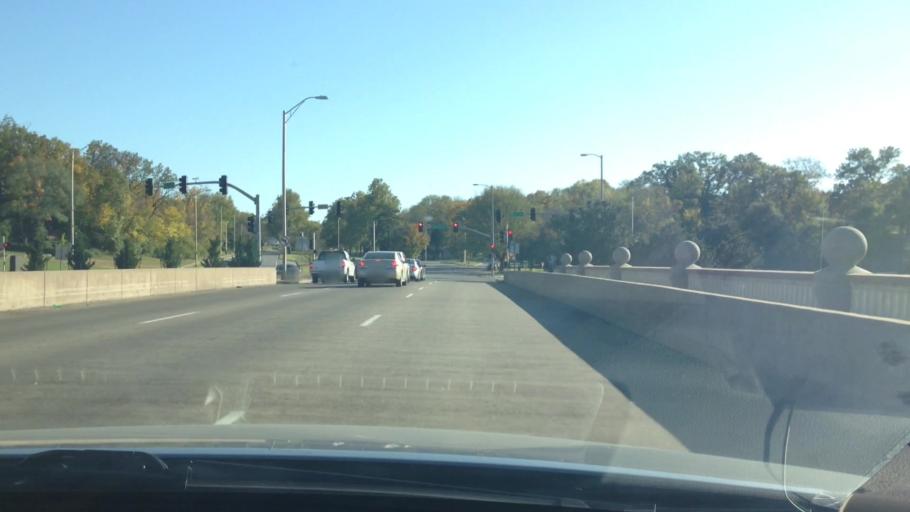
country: US
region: Kansas
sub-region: Johnson County
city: Westwood
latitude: 39.0406
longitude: -94.5685
